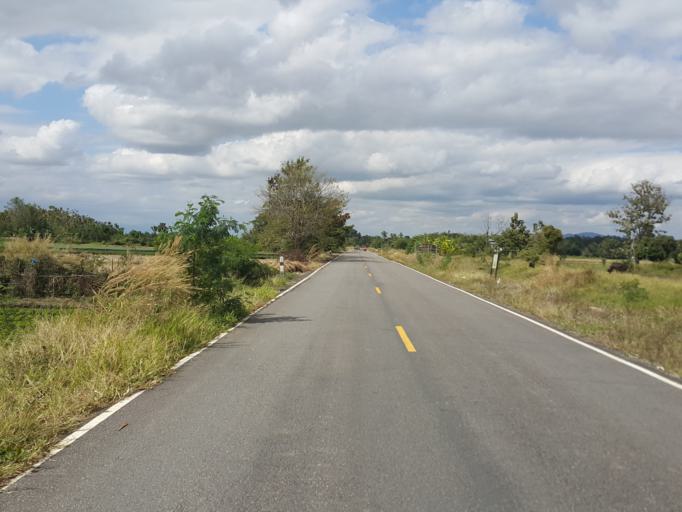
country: TH
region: Chiang Mai
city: Mae On
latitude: 18.8261
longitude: 99.1701
